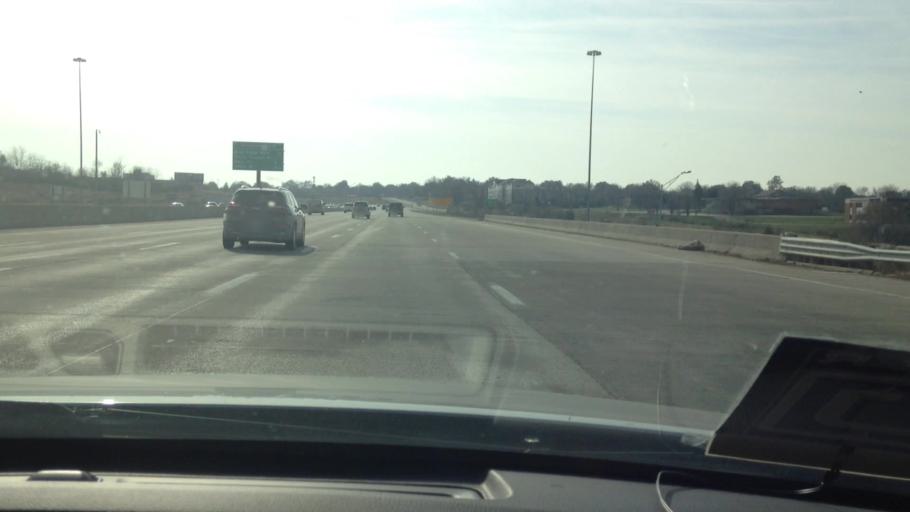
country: US
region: Missouri
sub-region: Jackson County
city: Grandview
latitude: 38.9254
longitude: -94.5286
